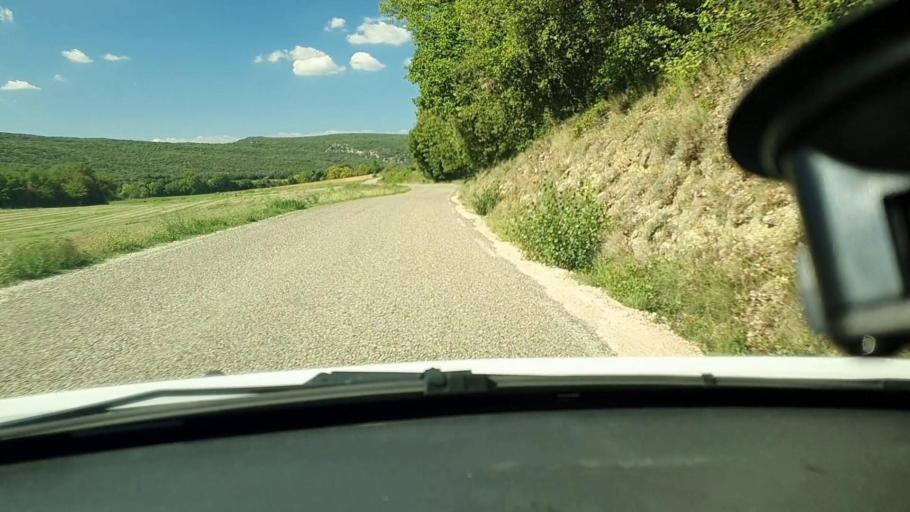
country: FR
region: Languedoc-Roussillon
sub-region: Departement du Gard
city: Goudargues
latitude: 44.1385
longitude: 4.4587
